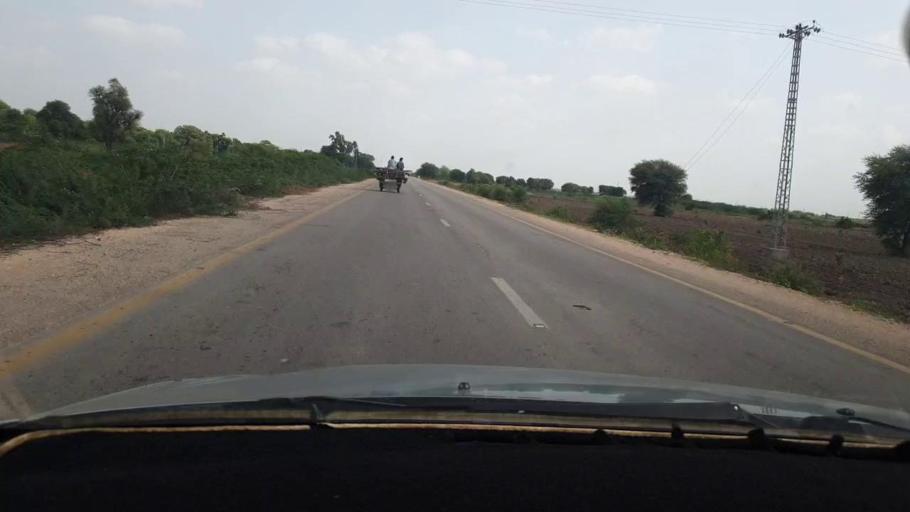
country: PK
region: Sindh
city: Digri
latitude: 25.0931
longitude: 69.1920
